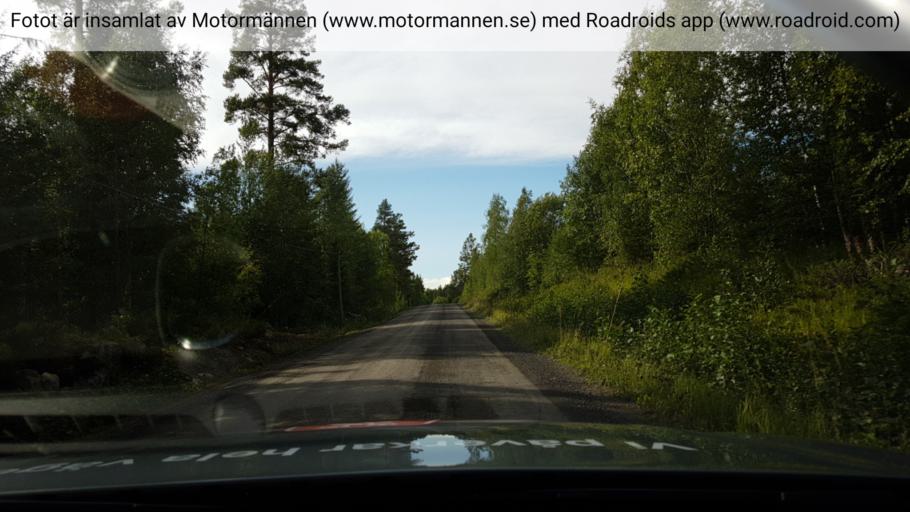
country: SE
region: Jaemtland
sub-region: Braecke Kommun
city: Braecke
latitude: 63.1972
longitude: 15.4636
